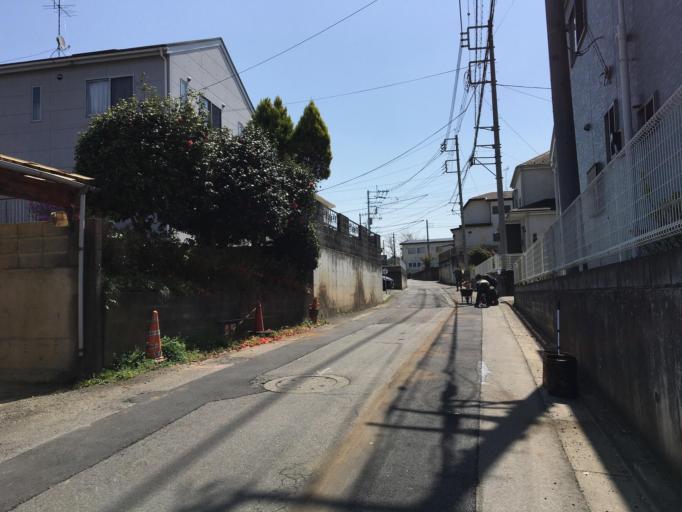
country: JP
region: Saitama
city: Sayama
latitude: 35.8946
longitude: 139.3679
